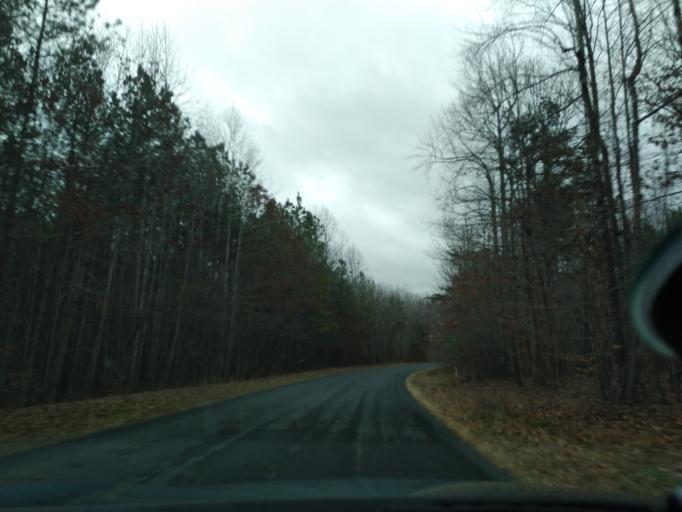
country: US
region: Virginia
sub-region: Appomattox County
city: Appomattox
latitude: 37.3991
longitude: -78.6614
